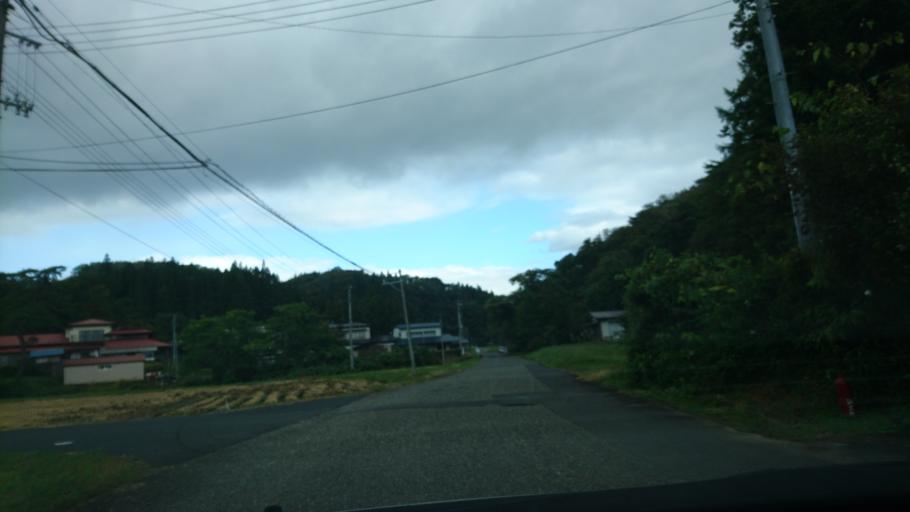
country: JP
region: Iwate
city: Ichinoseki
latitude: 38.9025
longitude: 141.0825
